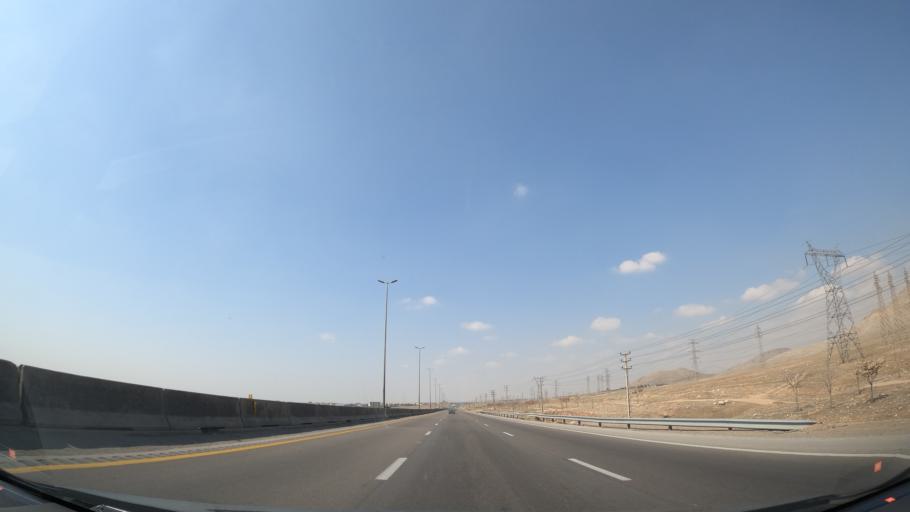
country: IR
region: Qazvin
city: Abyek
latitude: 36.0567
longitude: 50.5056
